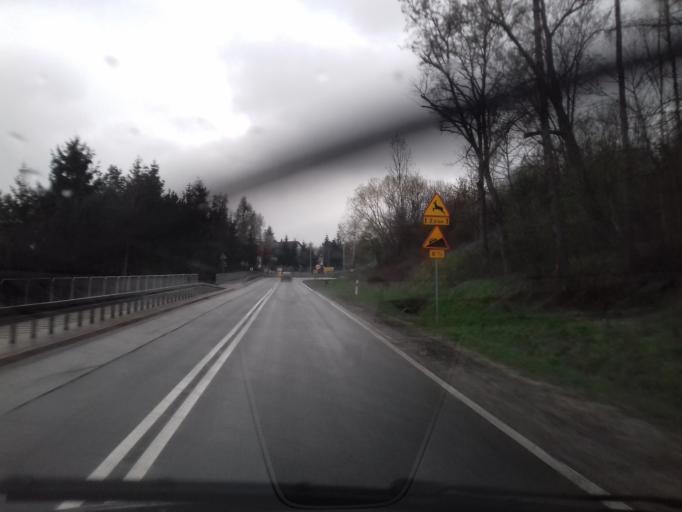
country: PL
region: Lesser Poland Voivodeship
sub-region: Powiat nowosadecki
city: Chelmiec
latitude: 49.6313
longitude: 20.6439
